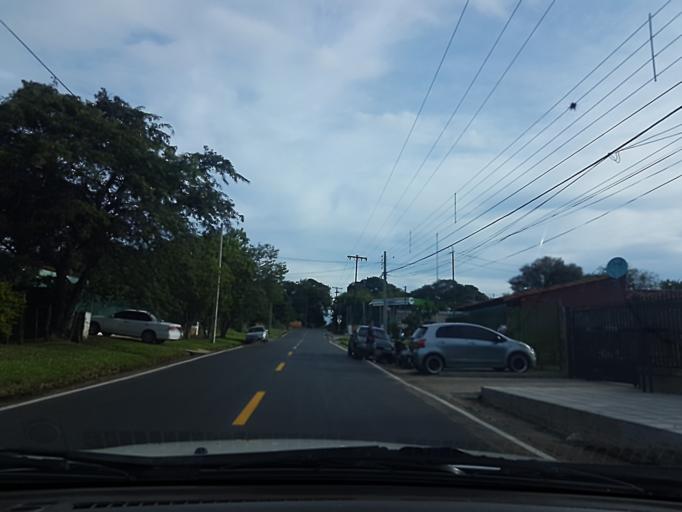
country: PY
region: Central
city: San Lorenzo
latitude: -25.2662
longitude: -57.4743
